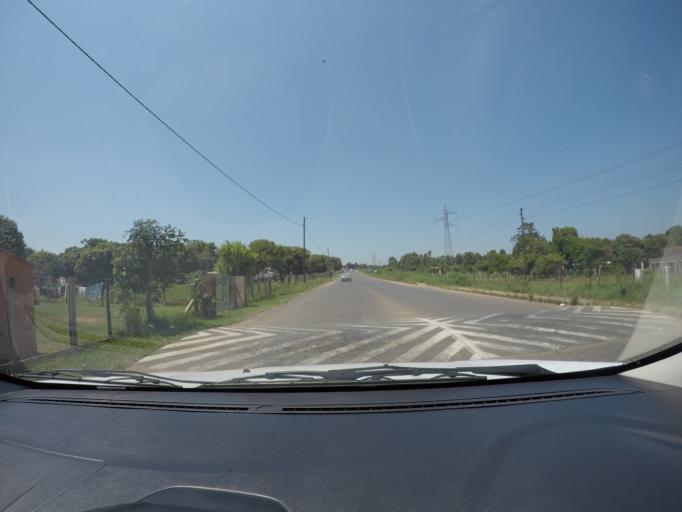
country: ZA
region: KwaZulu-Natal
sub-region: uThungulu District Municipality
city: eSikhawini
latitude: -28.8296
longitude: 31.9422
